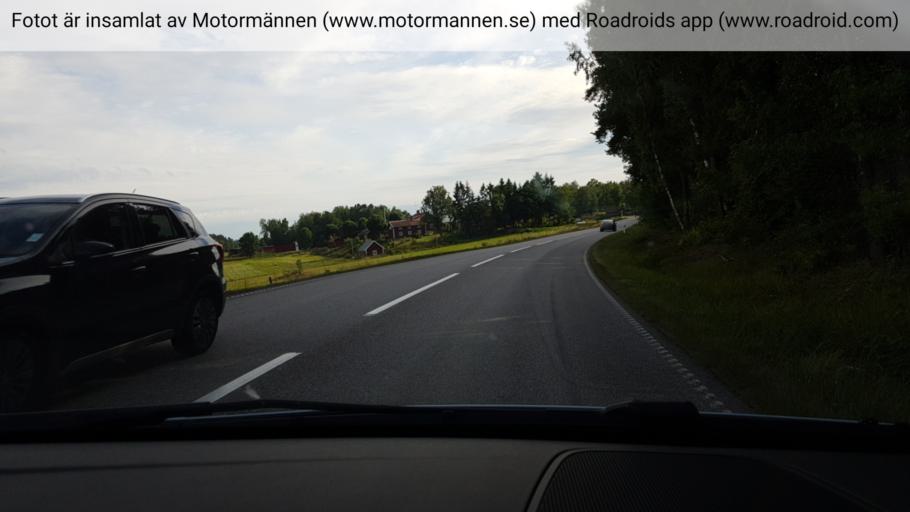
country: SE
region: Stockholm
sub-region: Norrtalje Kommun
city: Norrtalje
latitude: 59.8748
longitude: 18.7008
